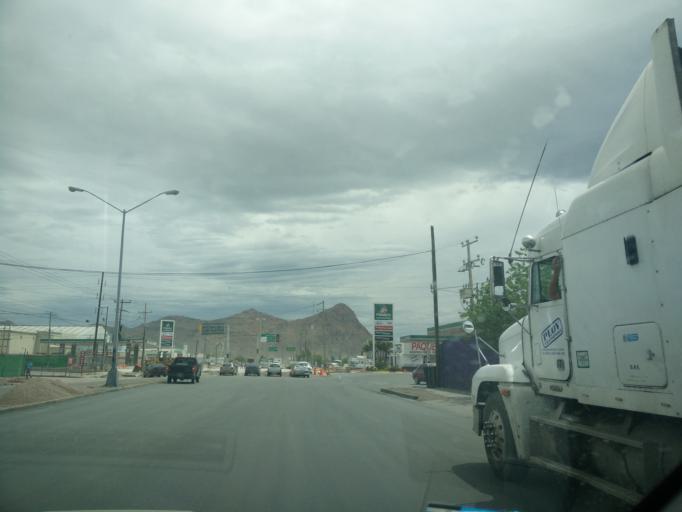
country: MX
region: Chihuahua
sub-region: Chihuahua
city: Chihuahua
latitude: 28.7119
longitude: -106.1063
